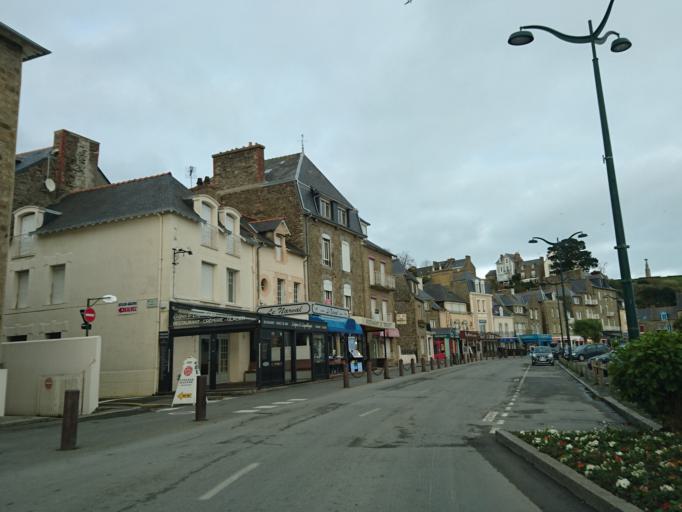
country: FR
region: Brittany
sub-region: Departement d'Ille-et-Vilaine
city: Cancale
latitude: 48.6708
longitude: -1.8552
